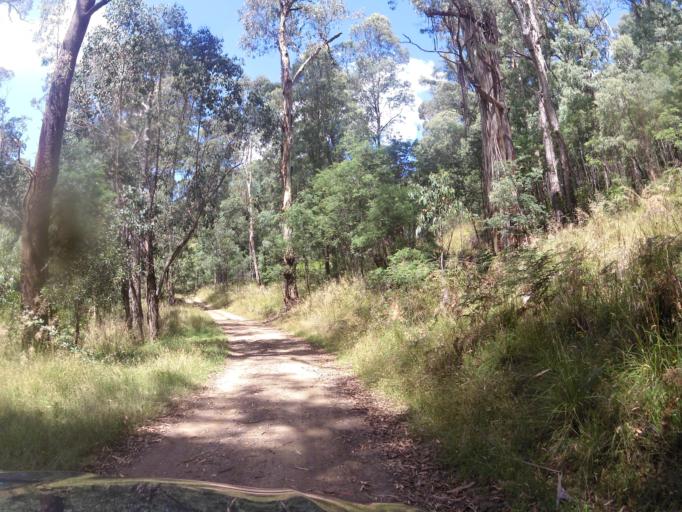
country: AU
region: Victoria
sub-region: Alpine
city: Mount Beauty
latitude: -36.8010
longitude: 147.0936
